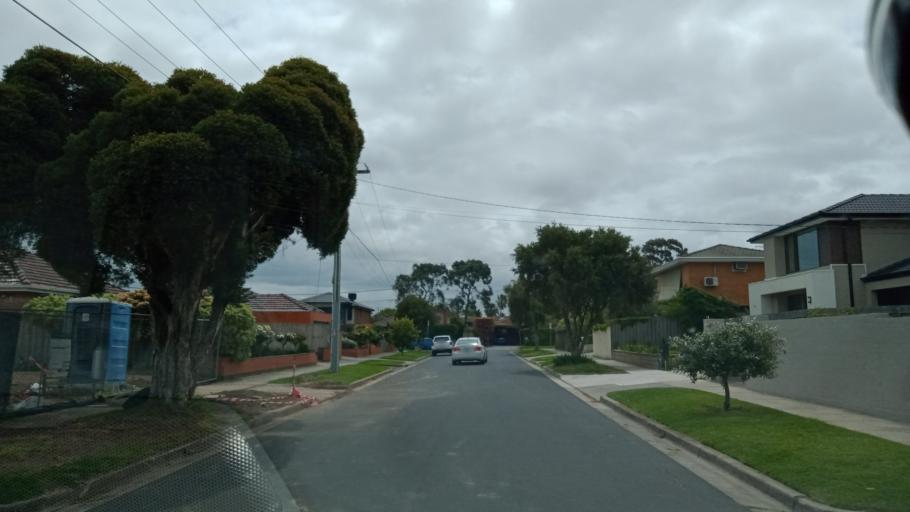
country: AU
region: Victoria
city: McKinnon
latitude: -37.9244
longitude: 145.0684
